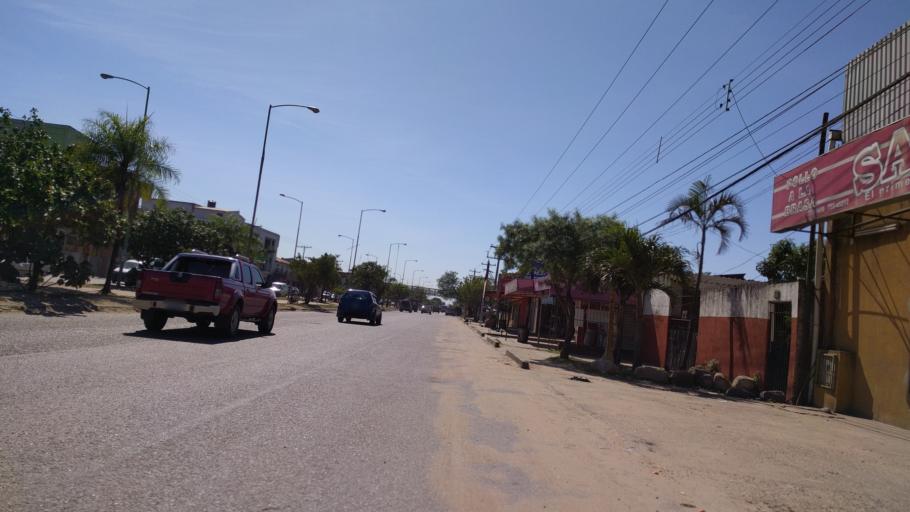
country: BO
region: Santa Cruz
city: Santa Cruz de la Sierra
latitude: -17.8300
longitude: -63.2285
